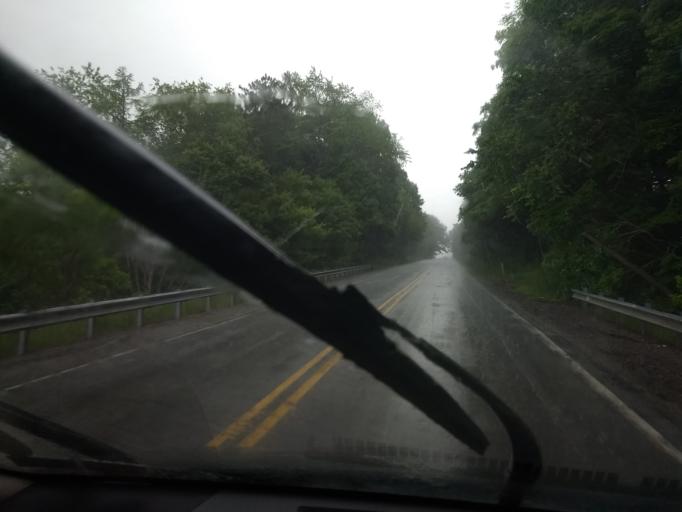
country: US
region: Pennsylvania
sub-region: Armstrong County
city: Apollo
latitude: 40.5229
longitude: -79.5883
